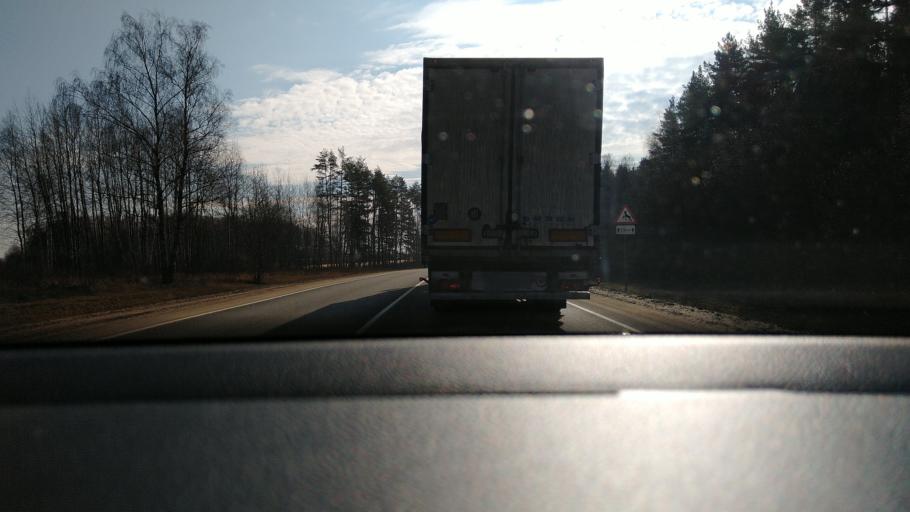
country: RU
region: Moskovskaya
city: Dubrovitsy
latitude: 55.3711
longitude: 37.4192
